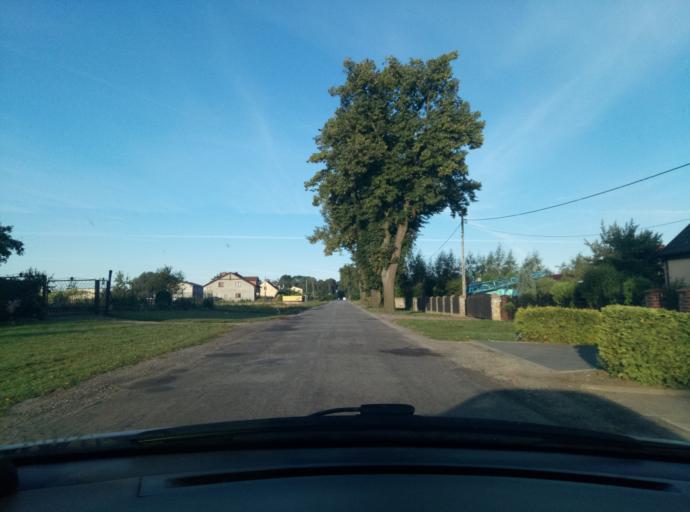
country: PL
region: Kujawsko-Pomorskie
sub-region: Powiat brodnicki
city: Jablonowo Pomorskie
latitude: 53.4002
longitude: 19.1664
